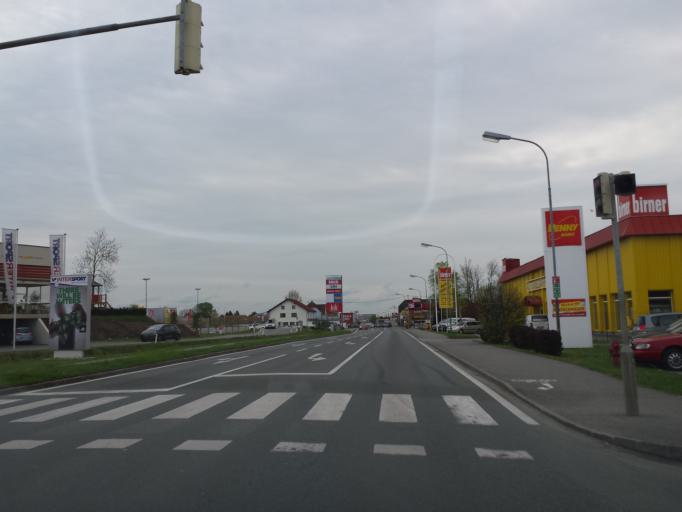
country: AT
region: Styria
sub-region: Politischer Bezirk Hartberg-Fuerstenfeld
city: Fuerstenfeld
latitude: 47.0584
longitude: 16.0682
